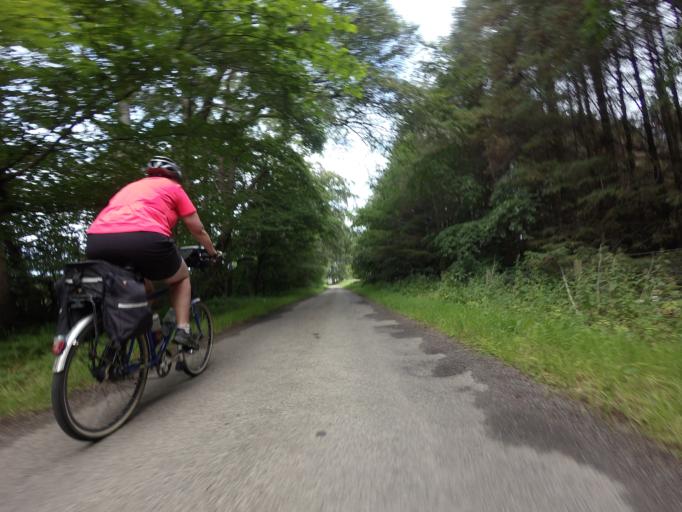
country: GB
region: Scotland
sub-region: Moray
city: Hopeman
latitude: 57.6717
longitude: -3.3993
